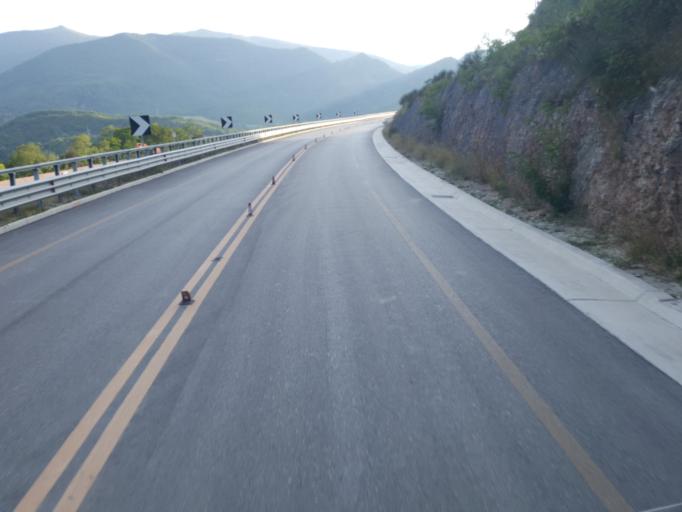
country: IT
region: The Marches
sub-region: Provincia di Ancona
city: Fabriano
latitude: 43.3047
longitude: 12.8417
